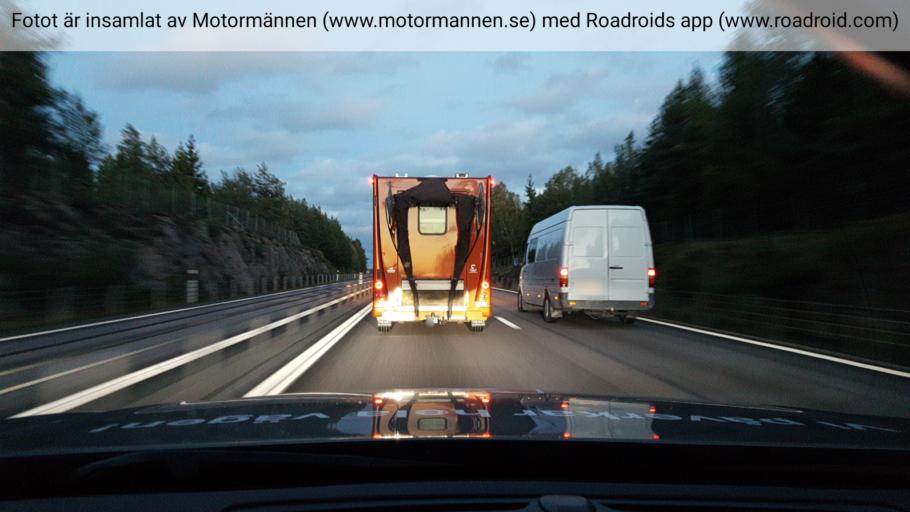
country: SE
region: Vaermland
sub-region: Karlstads Kommun
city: Skattkarr
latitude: 59.3928
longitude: 13.8276
